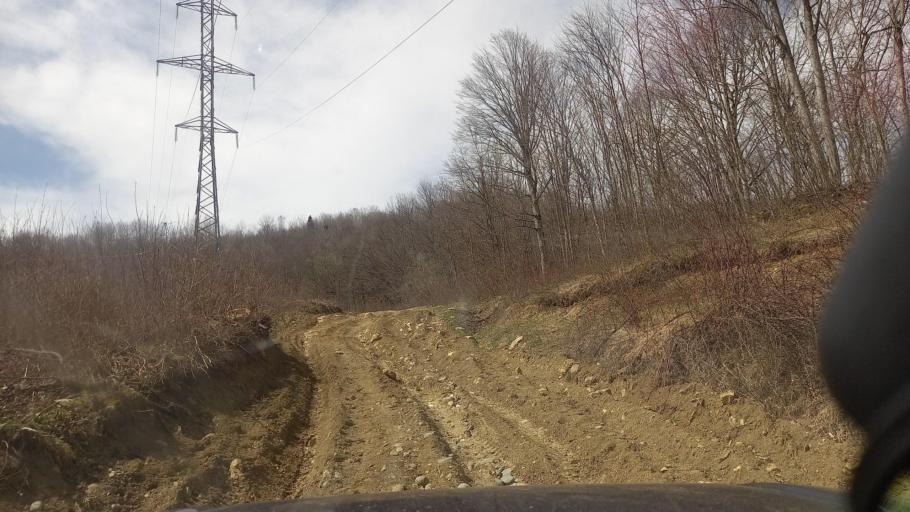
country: RU
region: Adygeya
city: Kamennomostskiy
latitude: 44.1112
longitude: 40.0938
